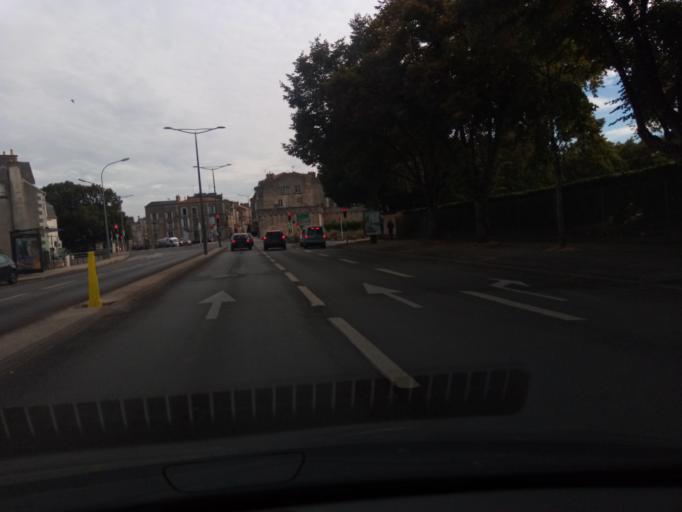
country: FR
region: Poitou-Charentes
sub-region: Departement de la Vienne
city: Poitiers
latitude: 46.5732
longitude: 0.3281
